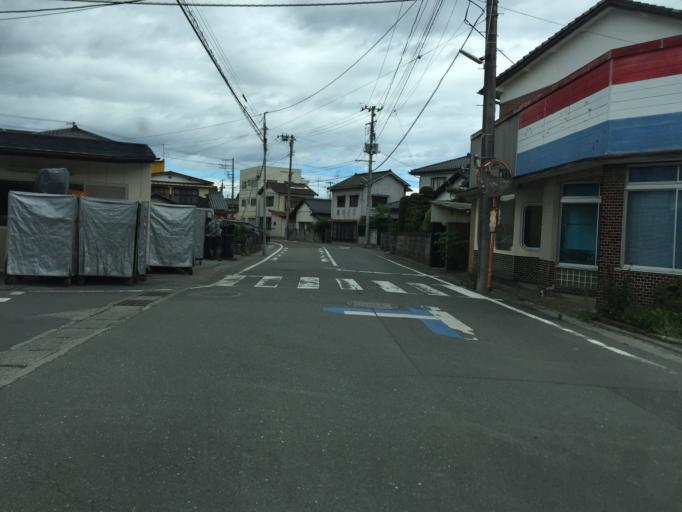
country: JP
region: Fukushima
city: Namie
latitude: 37.6330
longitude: 140.9643
